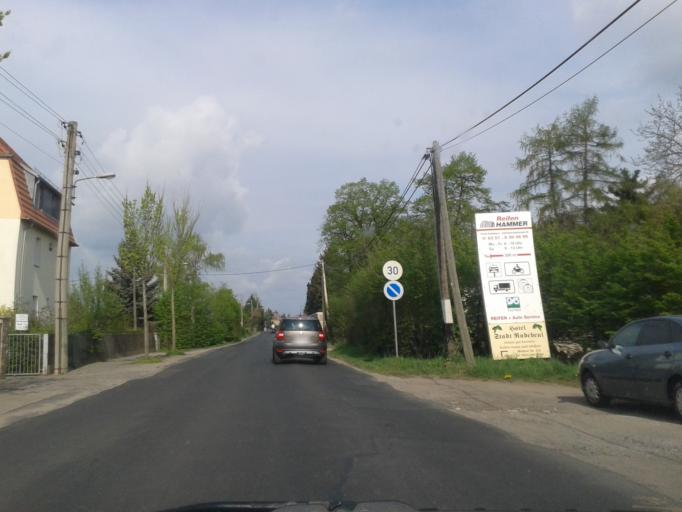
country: DE
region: Saxony
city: Radebeul
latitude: 51.1021
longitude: 13.6430
